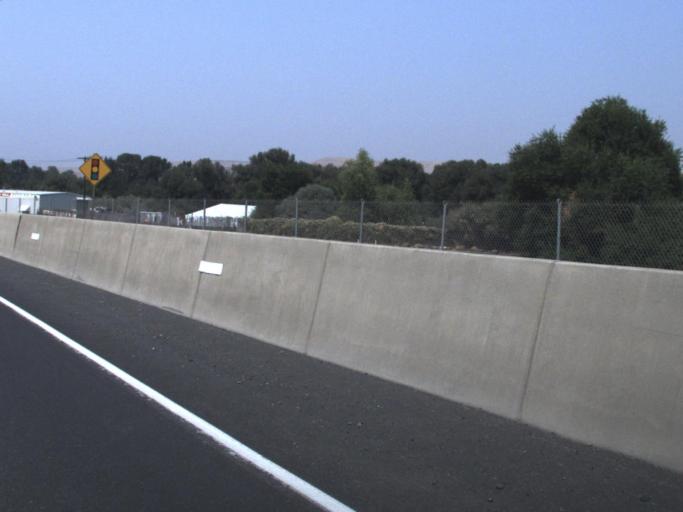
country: US
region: Washington
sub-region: Yakima County
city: Union Gap
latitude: 46.5836
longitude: -120.4644
